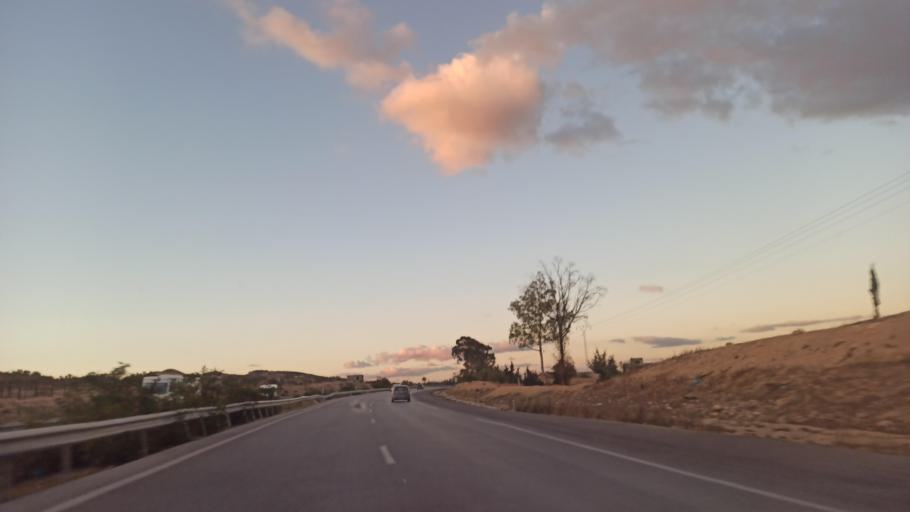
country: TN
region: Susah
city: Harqalah
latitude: 36.2285
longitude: 10.4137
